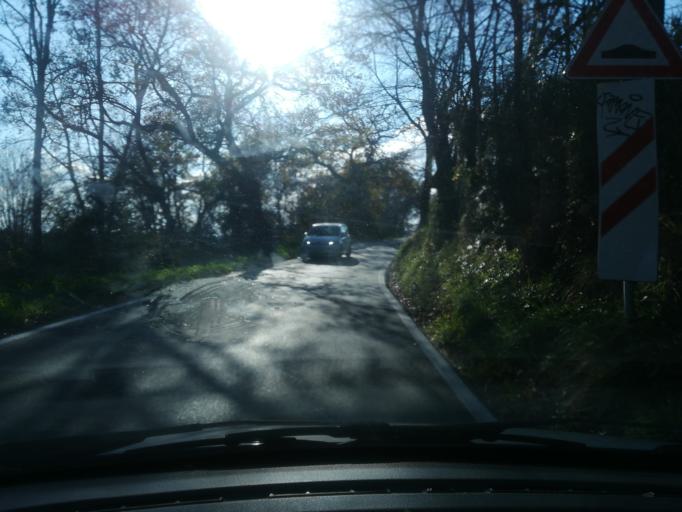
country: IT
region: The Marches
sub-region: Provincia di Macerata
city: Macerata
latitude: 43.2926
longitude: 13.4413
